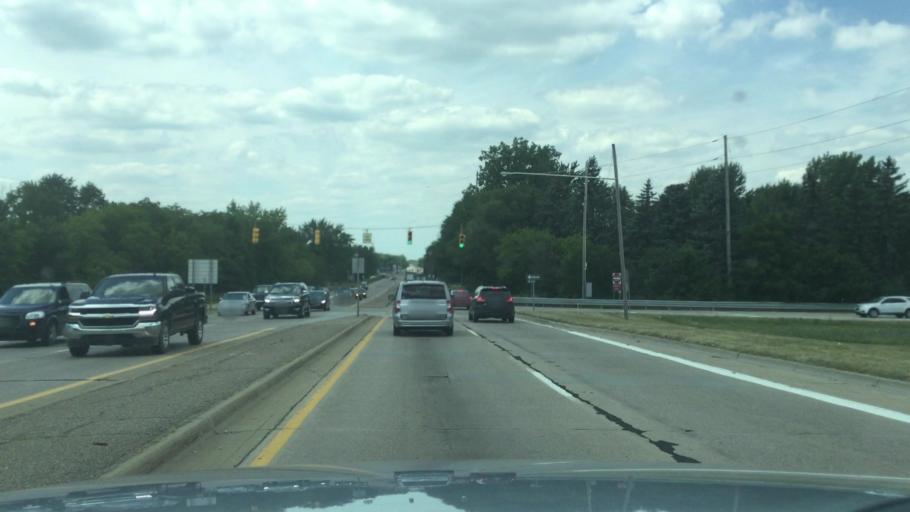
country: US
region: Michigan
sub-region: Genesee County
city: Grand Blanc
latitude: 42.9441
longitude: -83.6833
